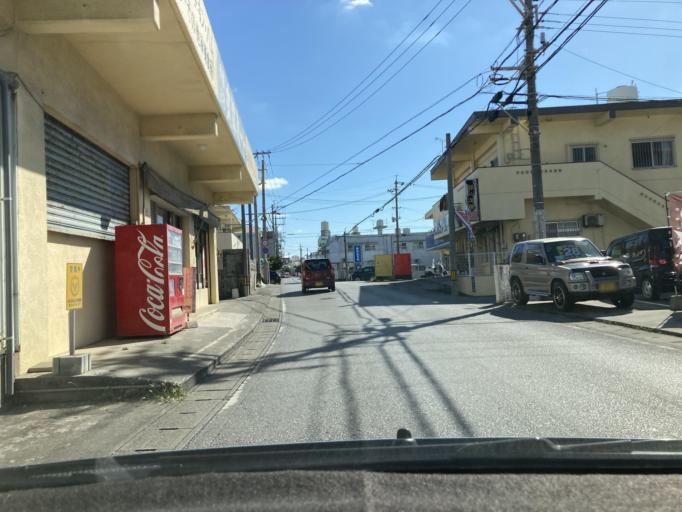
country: JP
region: Okinawa
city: Okinawa
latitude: 26.3517
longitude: 127.8246
